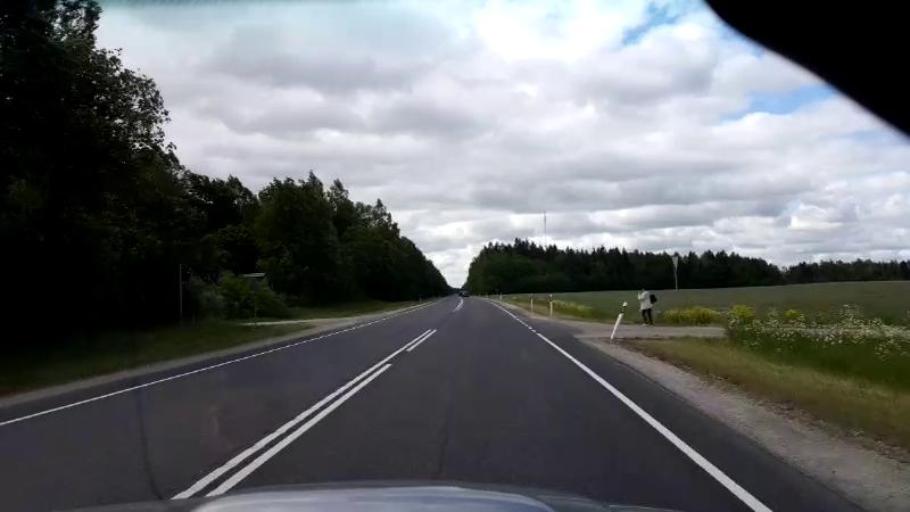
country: EE
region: Raplamaa
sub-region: Maerjamaa vald
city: Marjamaa
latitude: 58.9160
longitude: 24.4569
